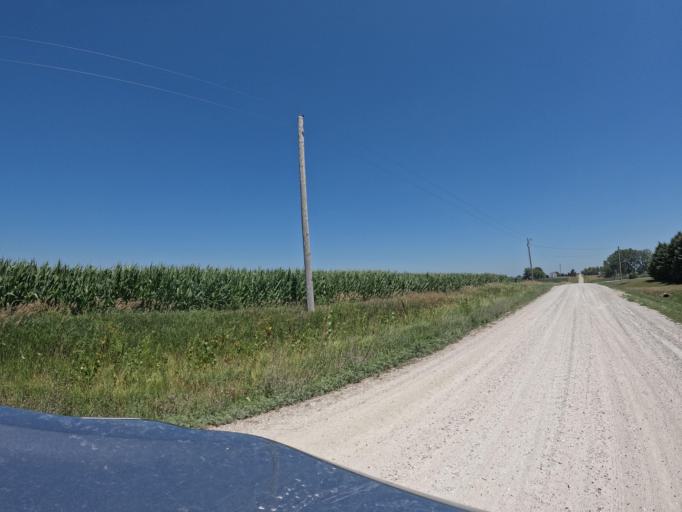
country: US
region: Iowa
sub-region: Keokuk County
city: Sigourney
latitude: 41.4234
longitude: -92.3542
